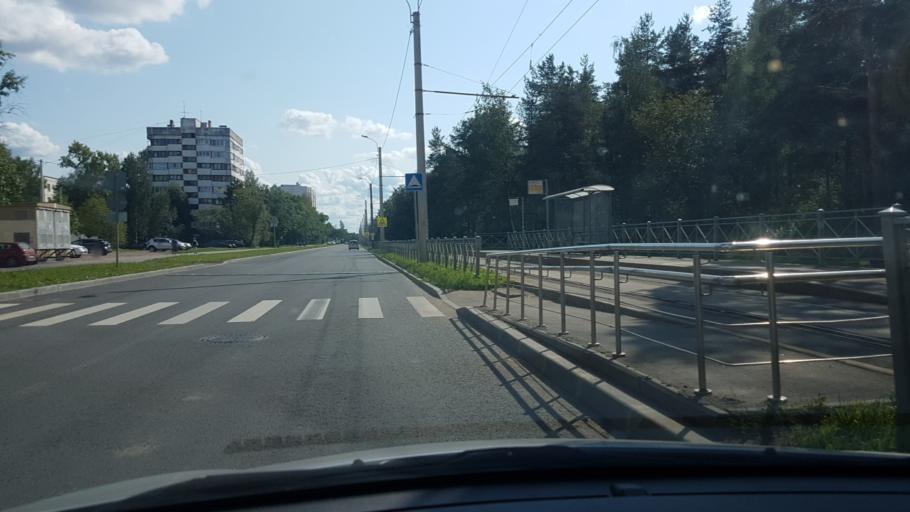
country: RU
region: St.-Petersburg
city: Sosnovaya Polyana
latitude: 59.8312
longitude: 30.1402
